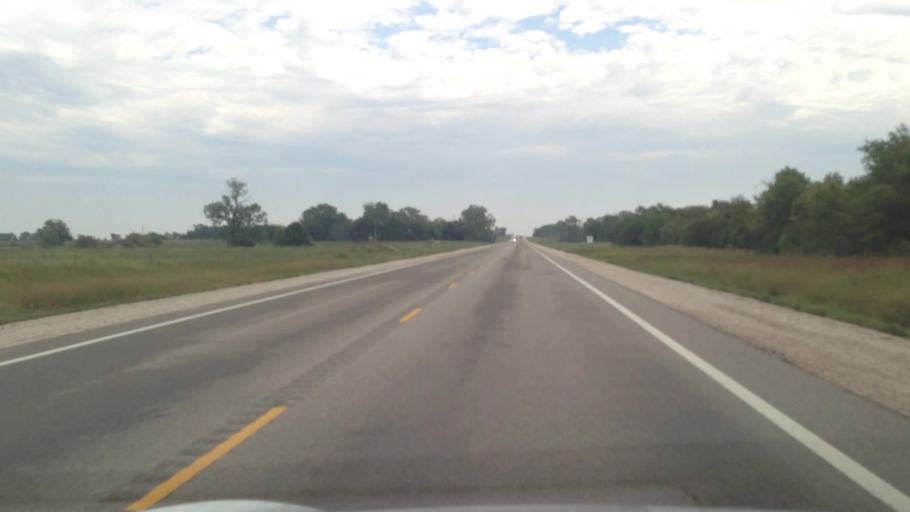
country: US
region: Kansas
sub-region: Allen County
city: Iola
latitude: 37.9102
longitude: -95.1210
